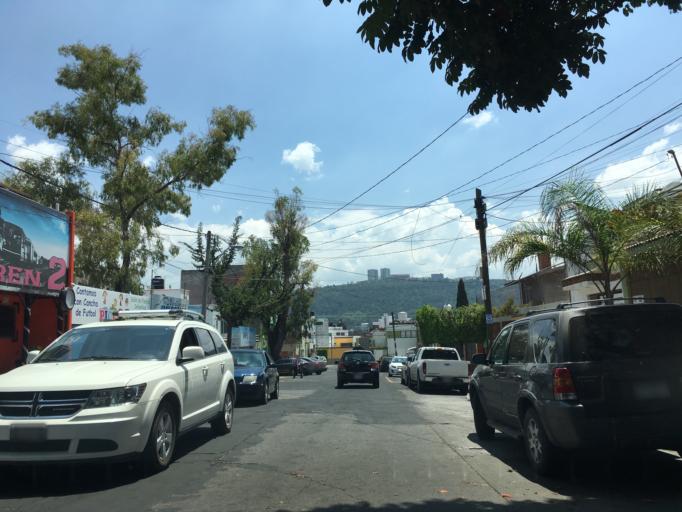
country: MX
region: Michoacan
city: Morelia
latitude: 19.6953
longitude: -101.1659
